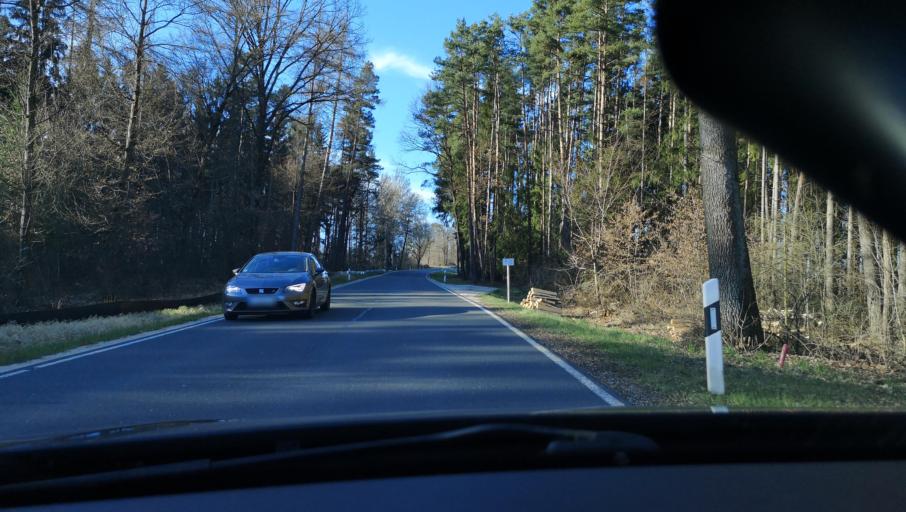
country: DE
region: Bavaria
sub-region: Upper Franconia
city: Michelau
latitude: 50.1843
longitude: 11.1191
